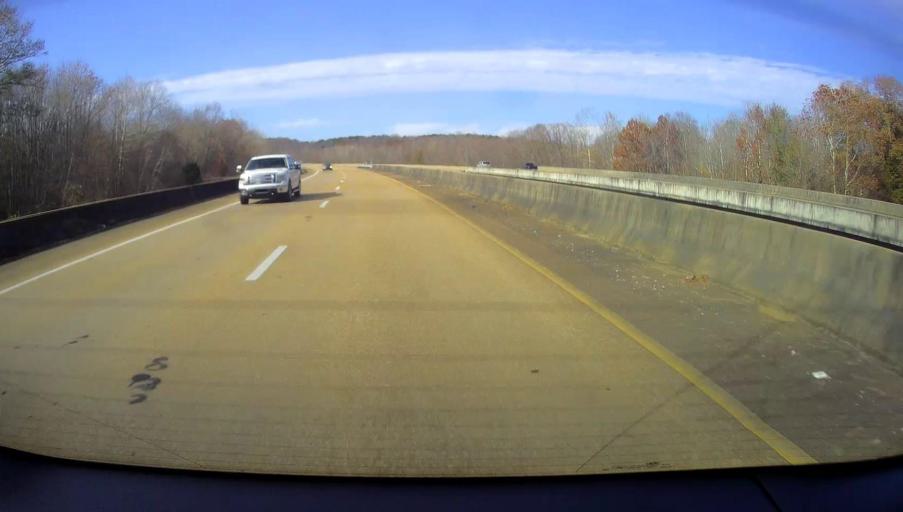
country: US
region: Mississippi
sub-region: Alcorn County
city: Corinth
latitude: 34.9435
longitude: -88.7852
